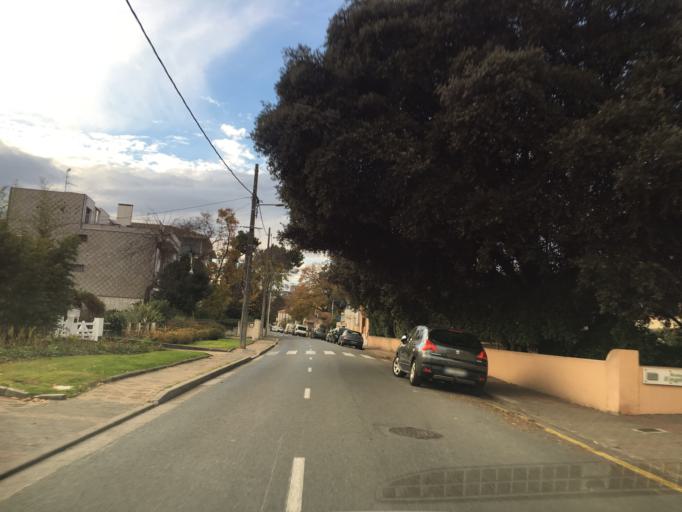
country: FR
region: Aquitaine
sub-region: Departement de la Gironde
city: Arcachon
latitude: 44.6625
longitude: -1.1601
